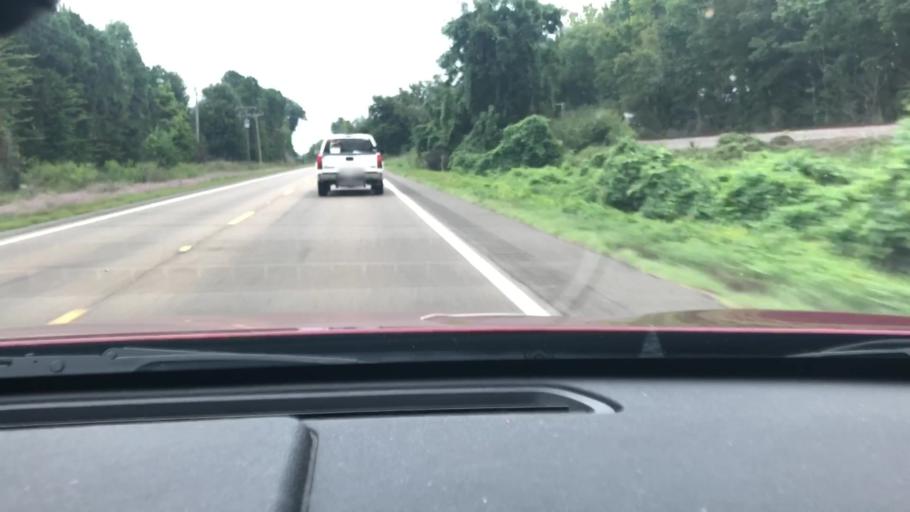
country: US
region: Arkansas
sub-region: Lafayette County
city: Lewisville
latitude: 33.3547
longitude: -93.6703
